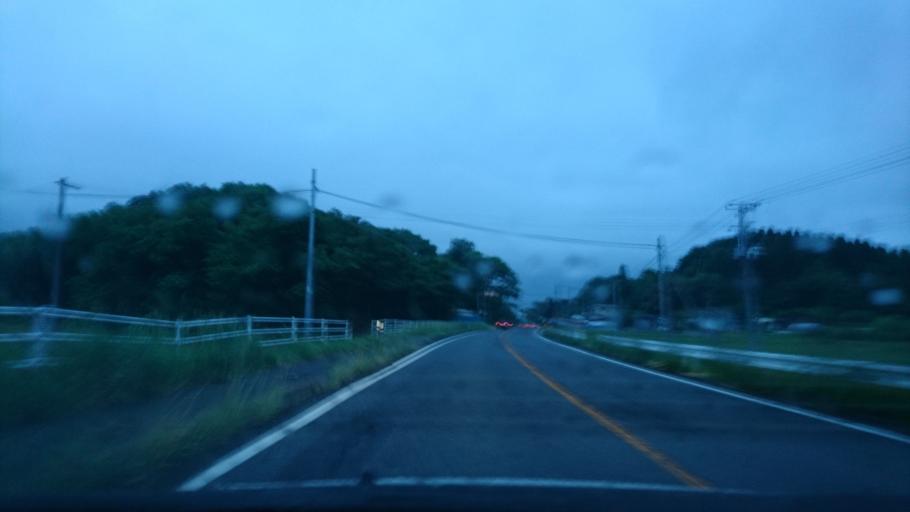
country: JP
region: Iwate
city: Ichinoseki
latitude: 38.7857
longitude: 141.0498
